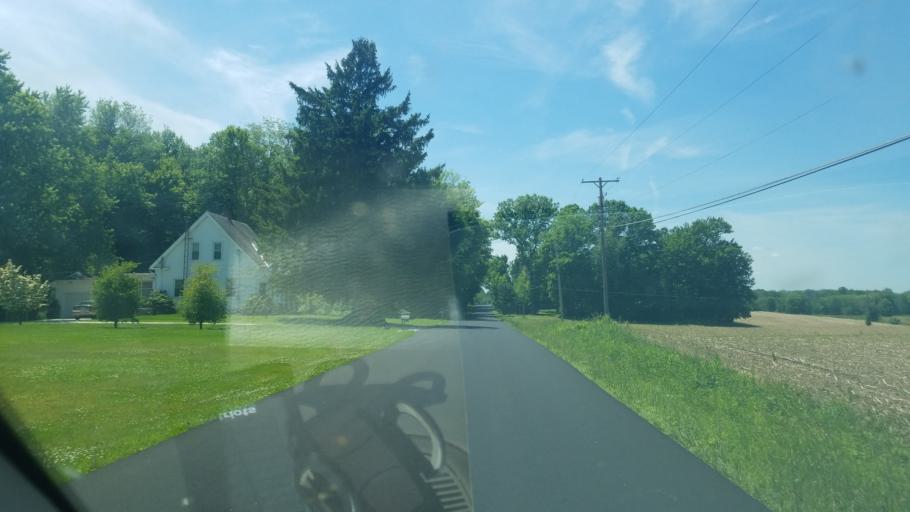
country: US
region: Ohio
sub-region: Stark County
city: Alliance
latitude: 40.8578
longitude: -81.1417
